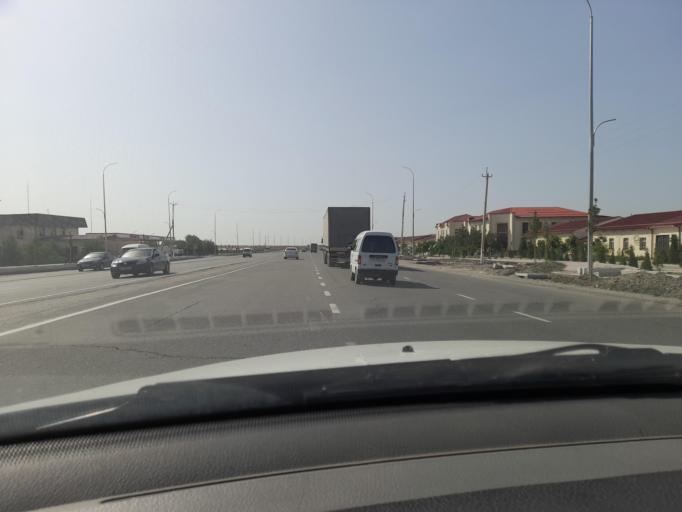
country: UZ
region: Samarqand
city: Daxbet
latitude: 39.7292
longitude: 66.9415
